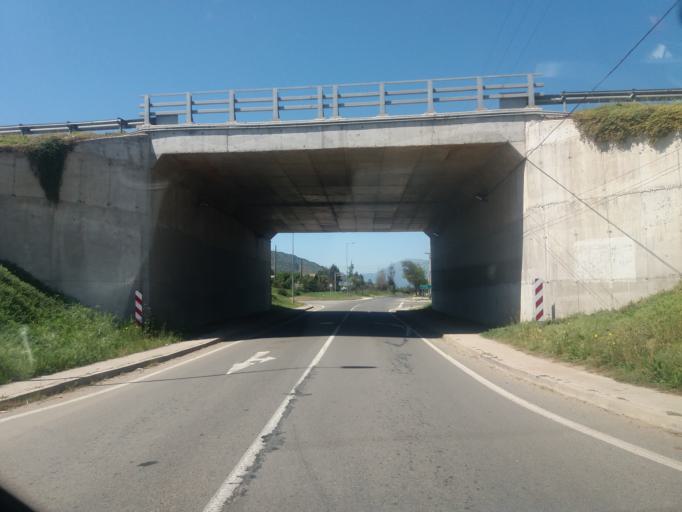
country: CL
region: Valparaiso
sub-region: Provincia de Marga Marga
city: Limache
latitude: -32.9714
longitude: -71.3014
